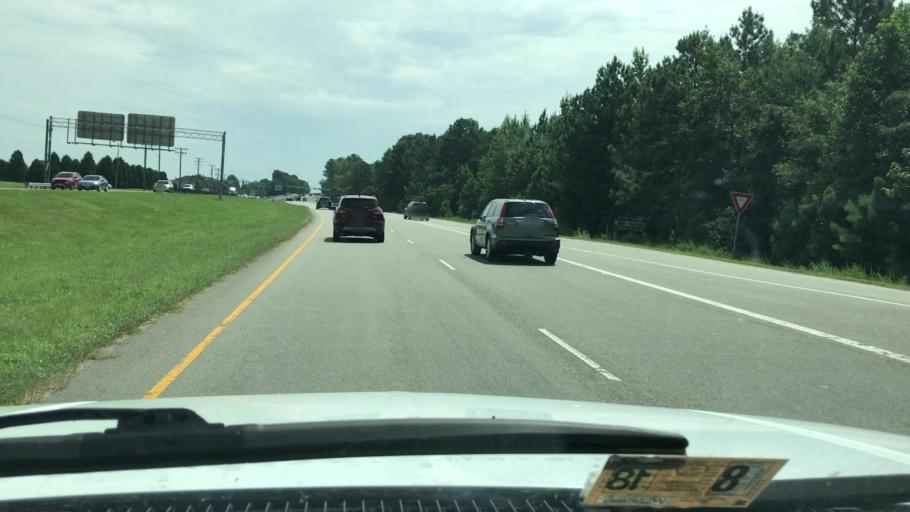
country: US
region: Virginia
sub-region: Chesterfield County
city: Brandermill
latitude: 37.5090
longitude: -77.6814
